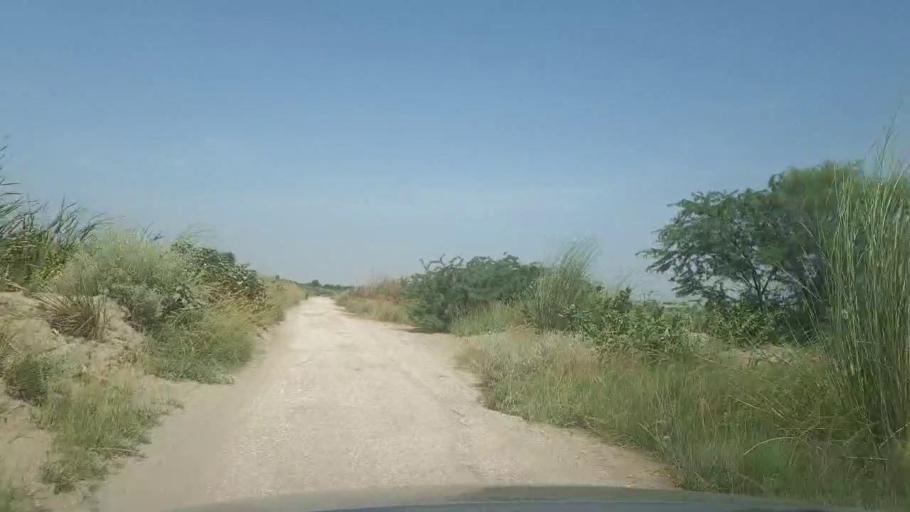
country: PK
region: Sindh
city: Khairpur
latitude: 27.3974
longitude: 69.0676
